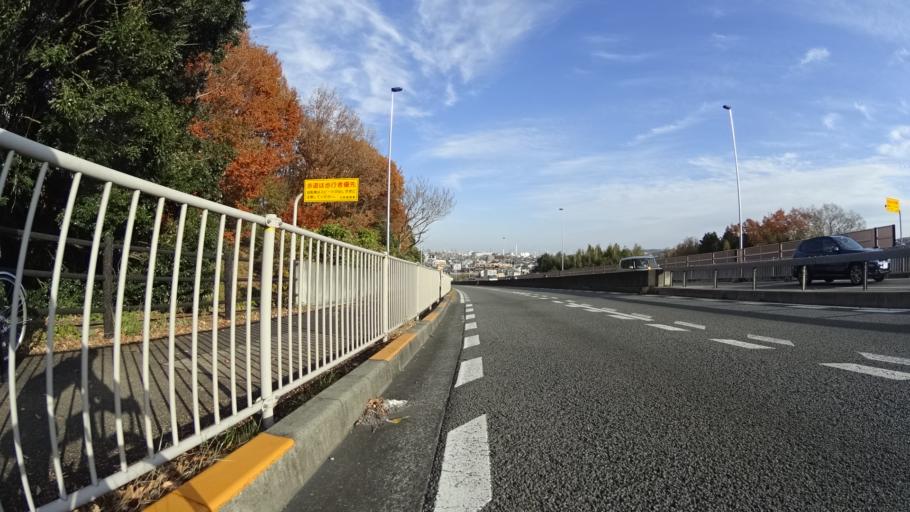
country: JP
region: Tokyo
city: Hino
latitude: 35.6688
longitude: 139.3967
